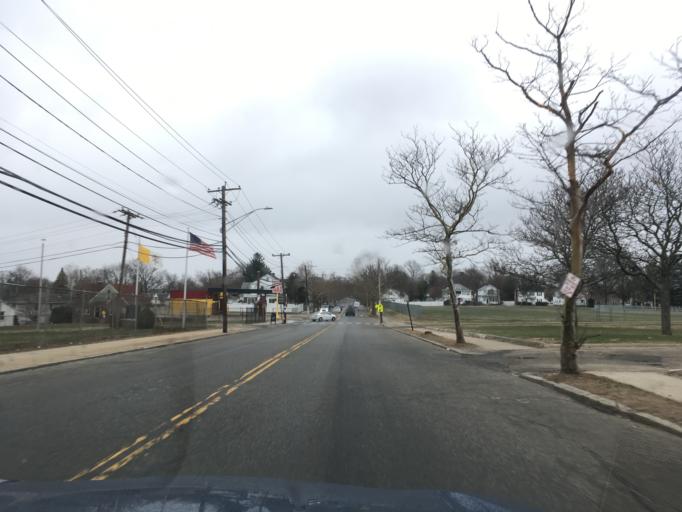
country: US
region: Rhode Island
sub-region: Providence County
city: North Providence
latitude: 41.8395
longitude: -71.4520
